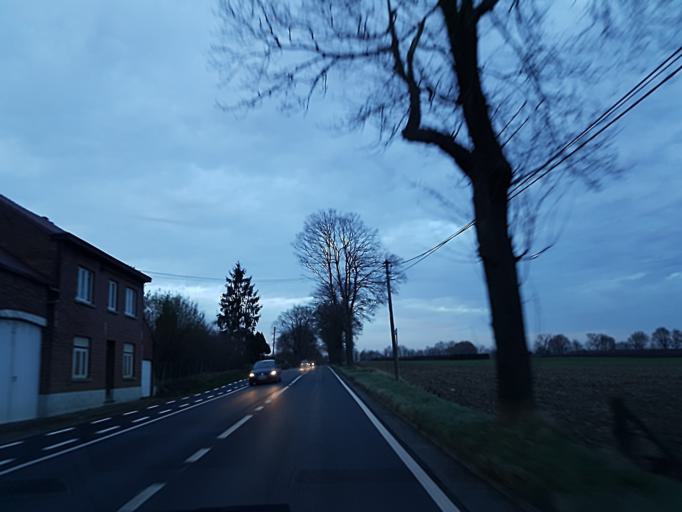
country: BE
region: Flanders
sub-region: Provincie Vlaams-Brabant
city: Lubbeek
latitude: 50.8934
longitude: 4.8782
